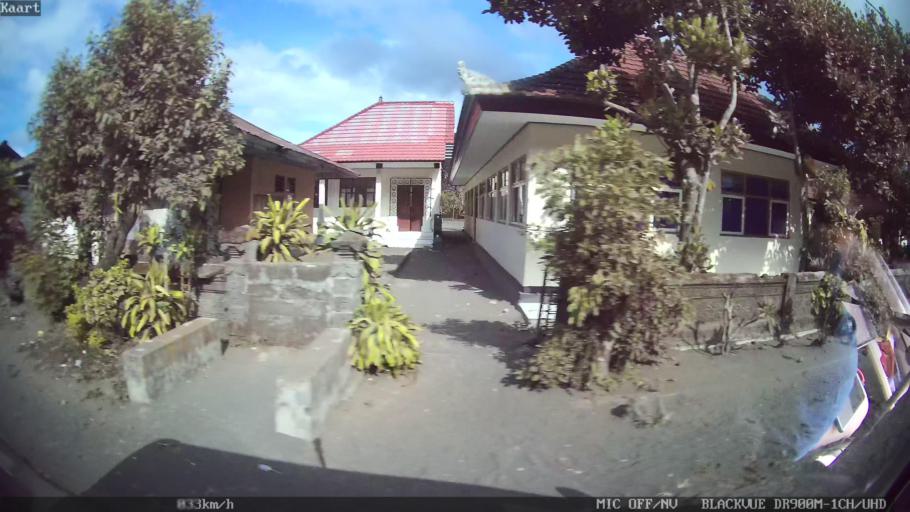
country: ID
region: Bali
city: Banjar Kedisan
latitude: -8.2207
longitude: 115.3629
